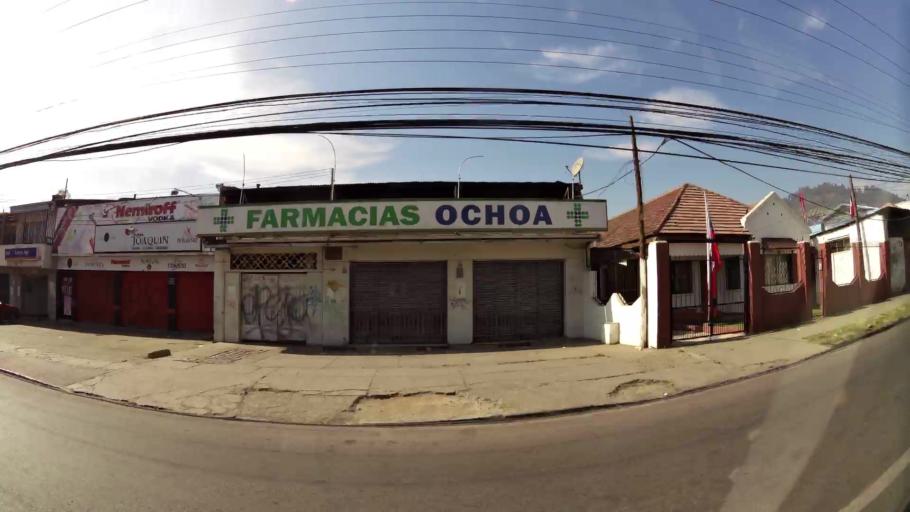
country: CL
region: Santiago Metropolitan
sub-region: Provincia de Santiago
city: Santiago
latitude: -33.4024
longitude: -70.6309
